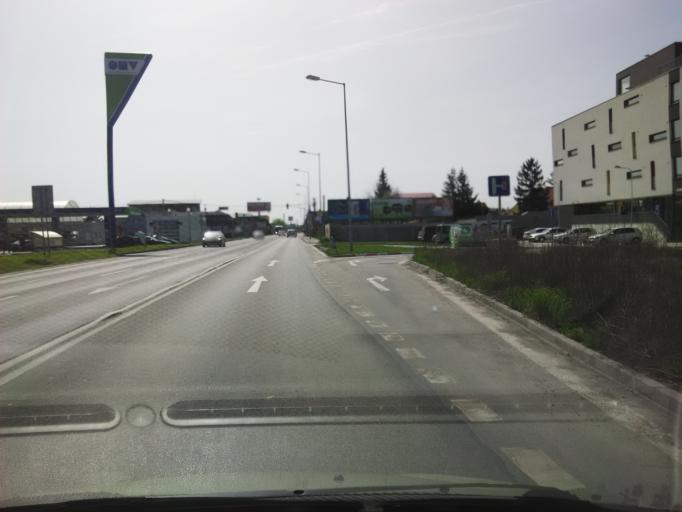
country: SK
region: Bratislavsky
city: Dunajska Luzna
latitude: 48.1385
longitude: 17.1935
